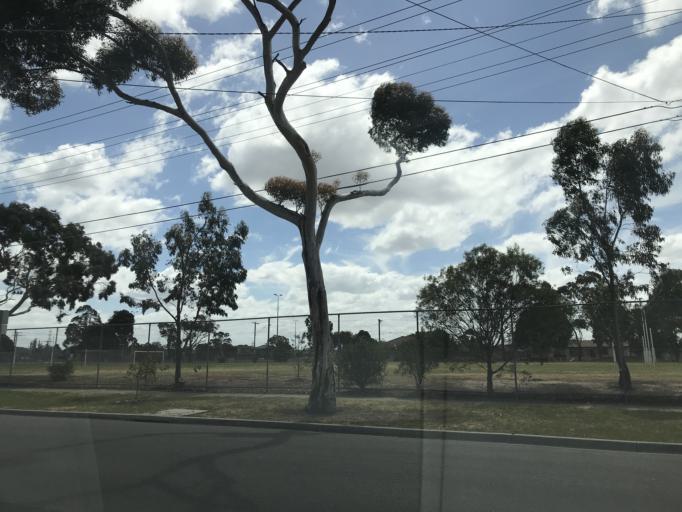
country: AU
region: Victoria
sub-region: Brimbank
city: Sunshine West
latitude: -37.7929
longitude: 144.8166
